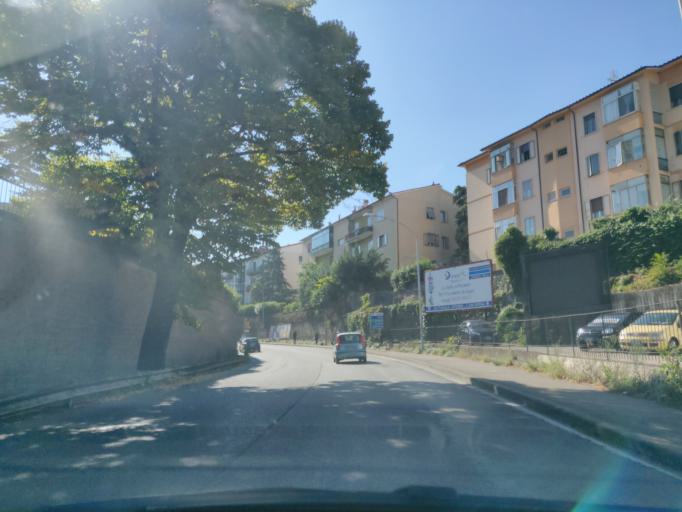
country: IT
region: Latium
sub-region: Provincia di Viterbo
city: Viterbo
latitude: 42.4255
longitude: 12.0993
